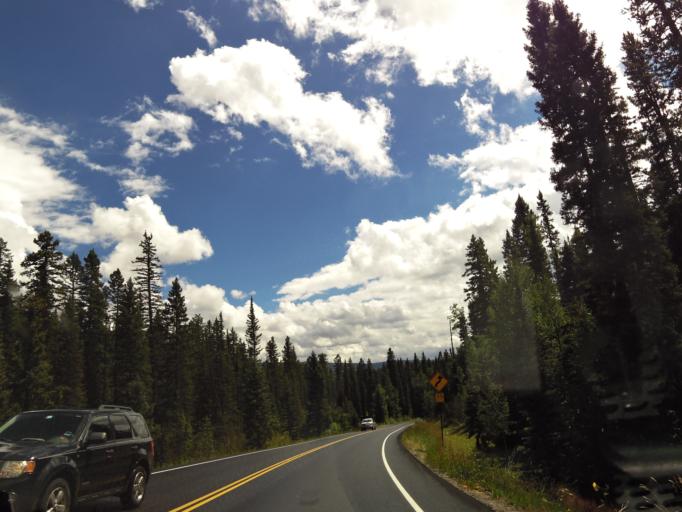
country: US
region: Colorado
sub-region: San Juan County
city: Silverton
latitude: 37.6760
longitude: -107.7910
